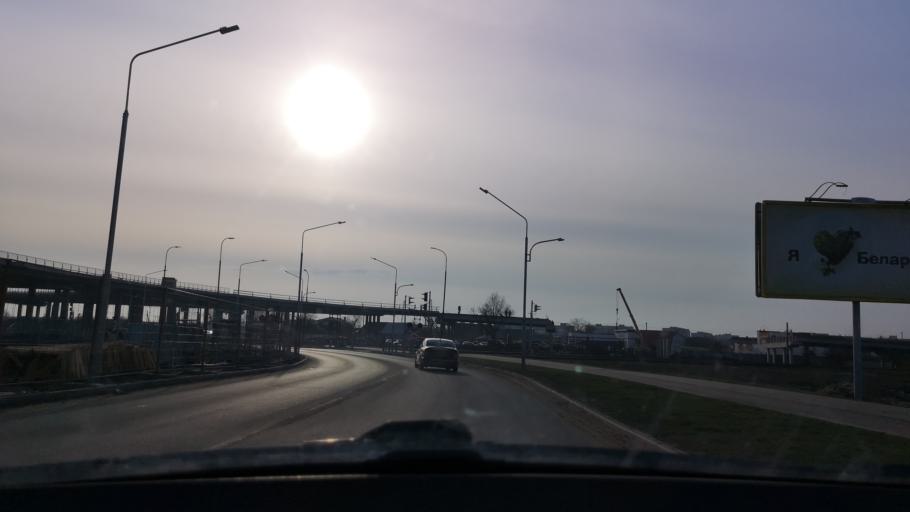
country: BY
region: Brest
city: Brest
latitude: 52.1067
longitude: 23.6656
